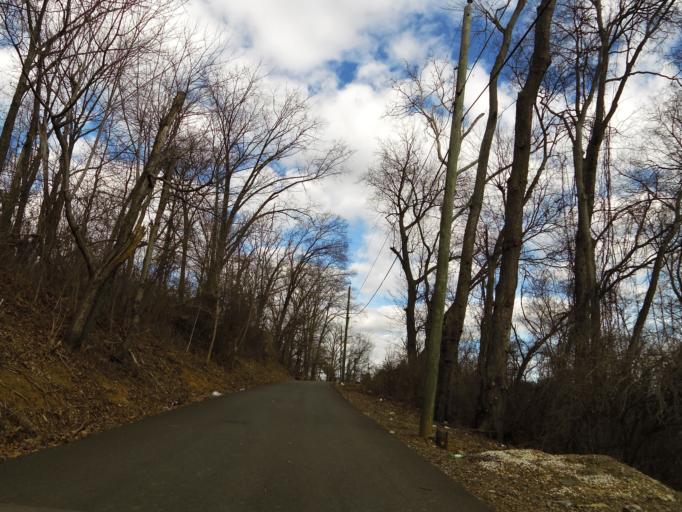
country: US
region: Tennessee
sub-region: Knox County
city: Knoxville
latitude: 35.9883
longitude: -83.9040
